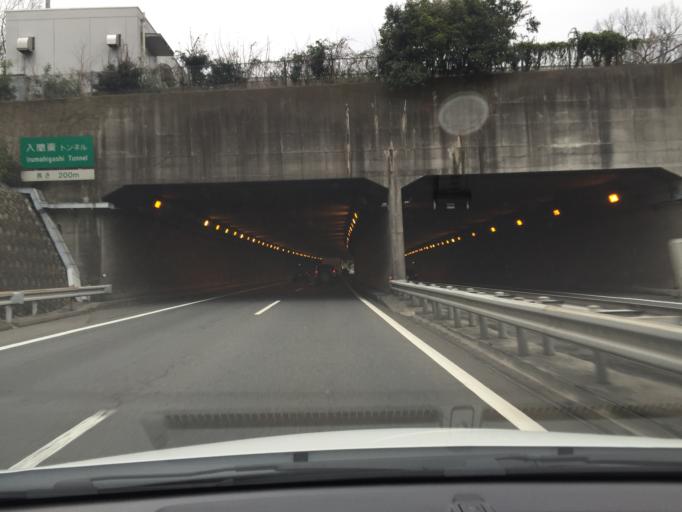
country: JP
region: Saitama
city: Sayama
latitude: 35.8342
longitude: 139.3734
